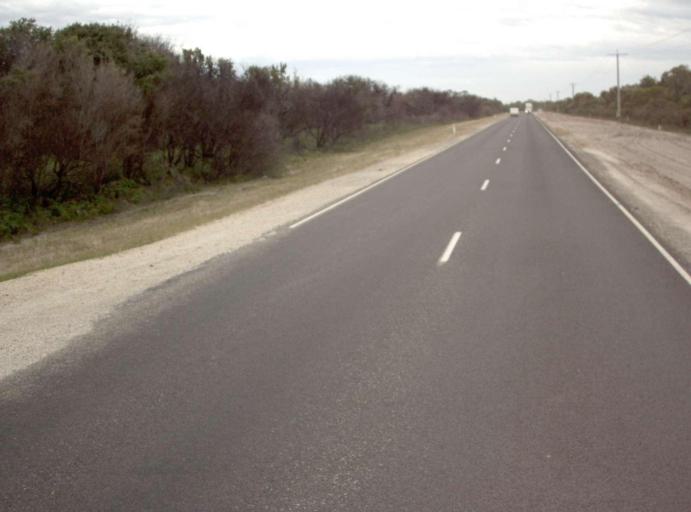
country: AU
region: Victoria
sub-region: East Gippsland
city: Bairnsdale
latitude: -38.0831
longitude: 147.5296
